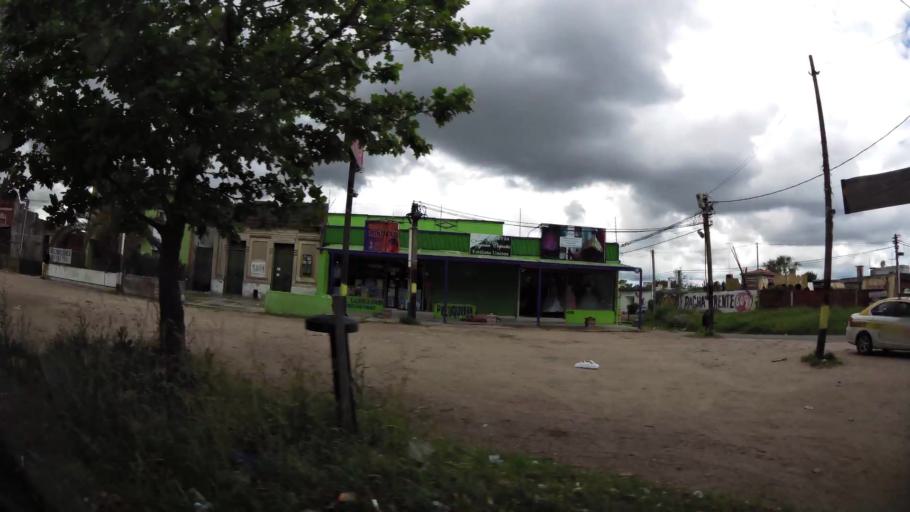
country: UY
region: Canelones
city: Toledo
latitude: -34.8210
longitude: -56.1400
